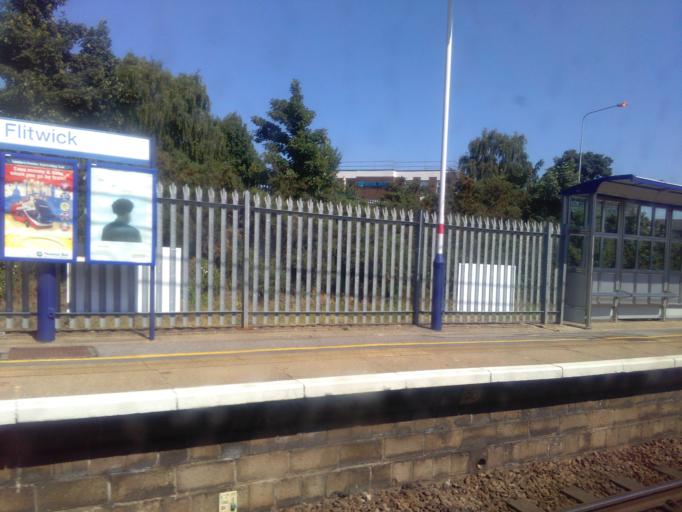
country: GB
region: England
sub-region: Central Bedfordshire
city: Flitwick
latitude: 52.0031
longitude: -0.4942
